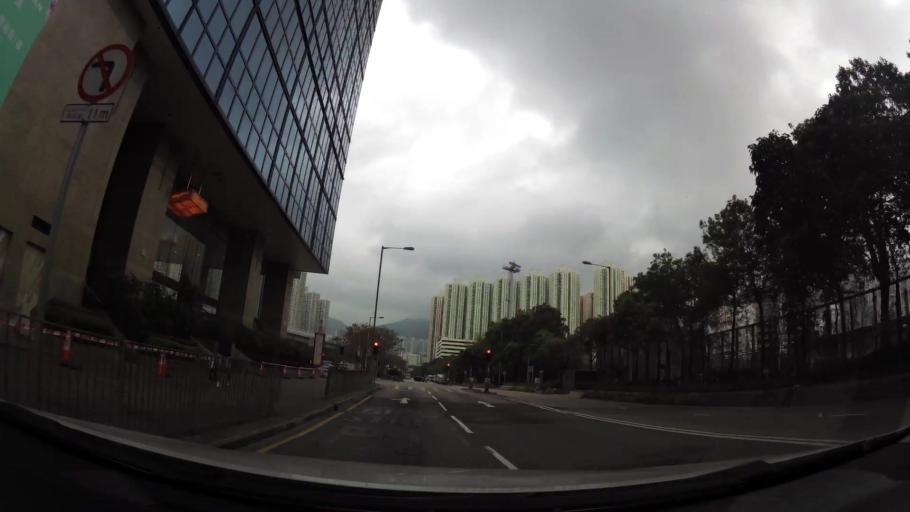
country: HK
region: Kowloon City
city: Kowloon
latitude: 22.3263
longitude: 114.2059
